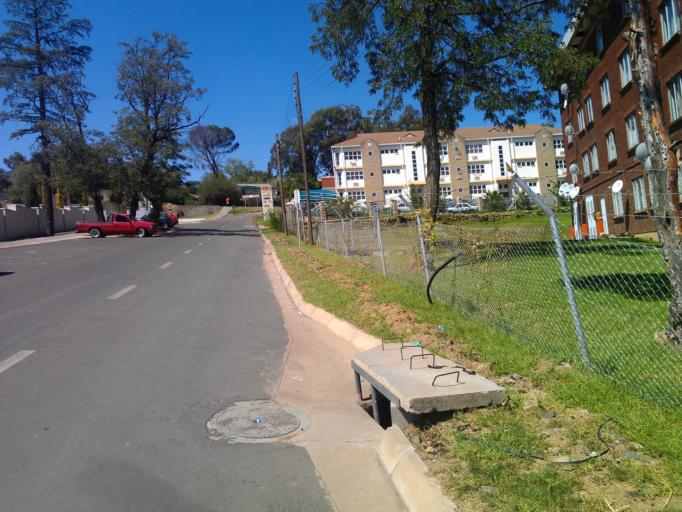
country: LS
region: Maseru
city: Maseru
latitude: -29.3107
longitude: 27.4773
